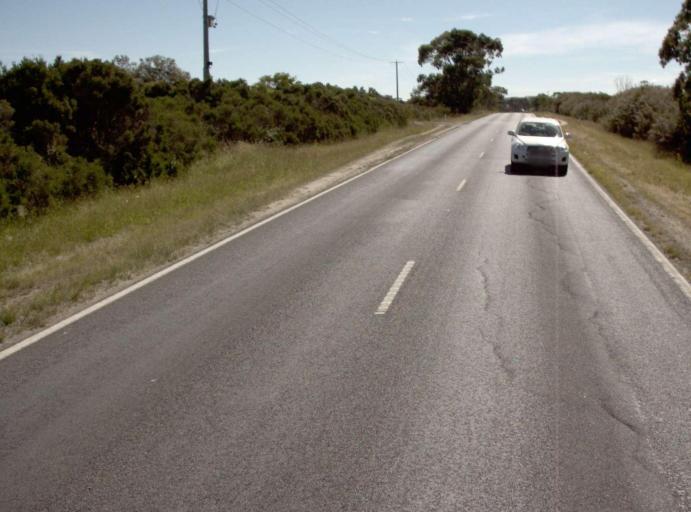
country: AU
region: Victoria
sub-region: Latrobe
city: Morwell
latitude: -38.6353
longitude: 146.5342
